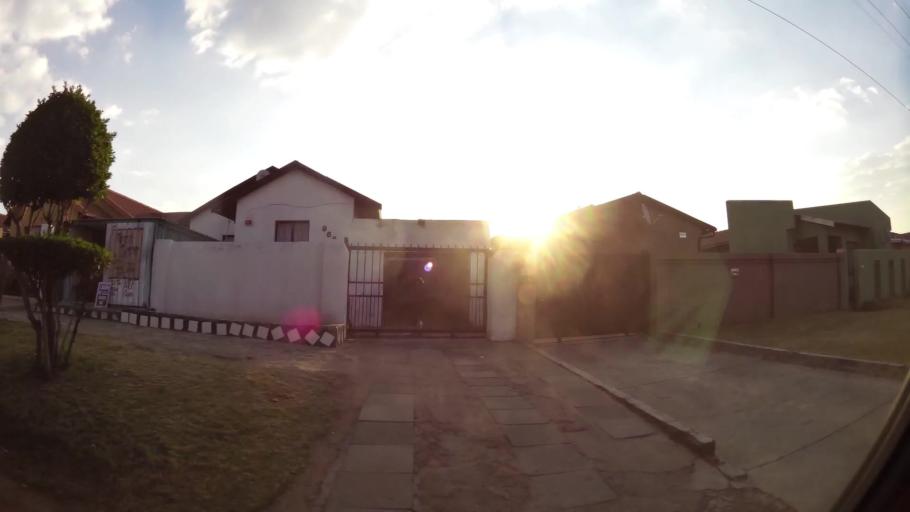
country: ZA
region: Gauteng
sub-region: City of Johannesburg Metropolitan Municipality
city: Soweto
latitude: -26.2305
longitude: 27.9044
